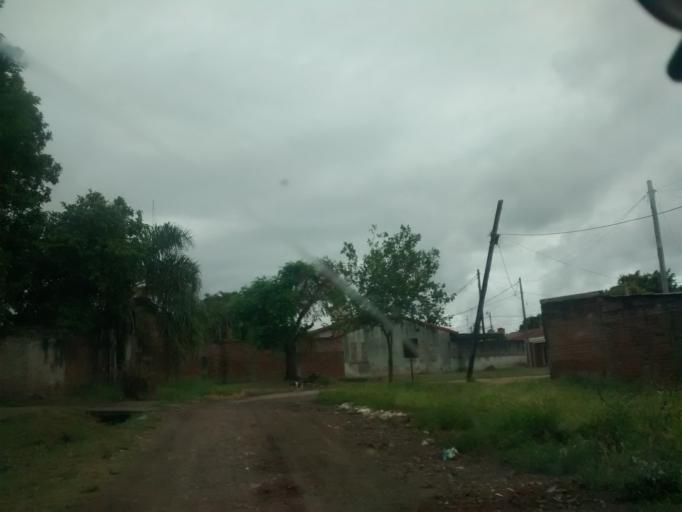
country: AR
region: Chaco
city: Resistencia
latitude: -27.4392
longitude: -58.9782
